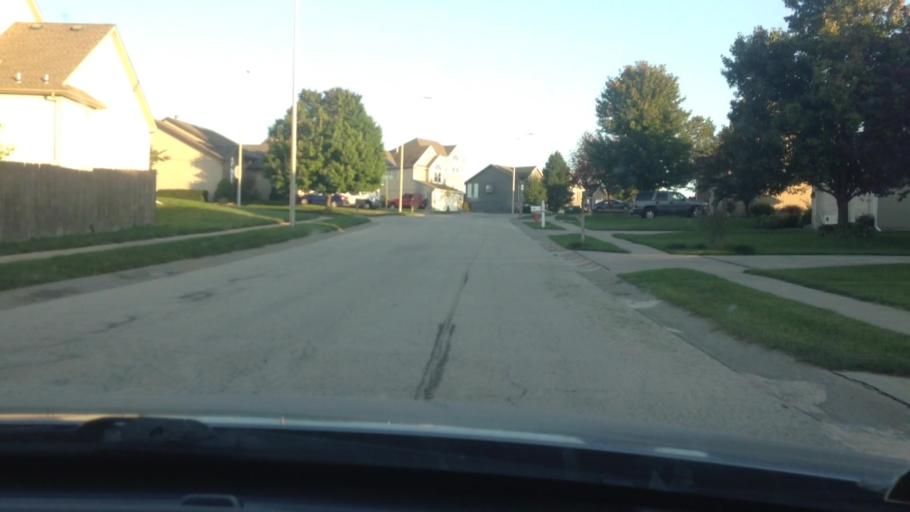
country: US
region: Missouri
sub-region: Clay County
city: Smithville
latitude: 39.3003
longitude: -94.5880
